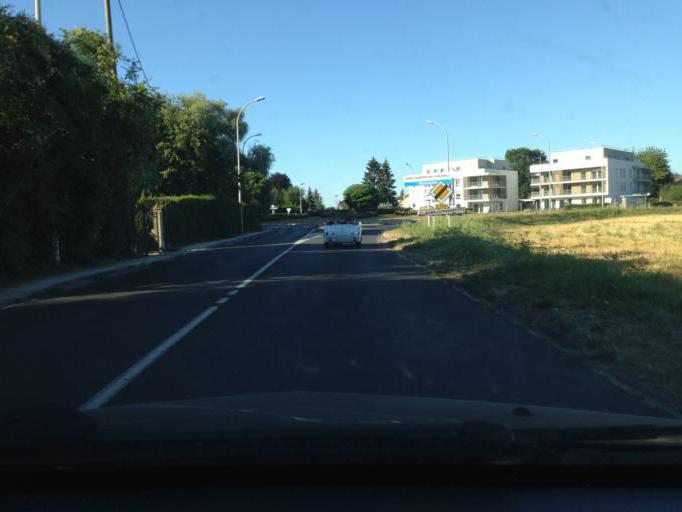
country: FR
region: Ile-de-France
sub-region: Departement des Yvelines
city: Saint-Remy-les-Chevreuse
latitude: 48.7191
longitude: 2.0875
